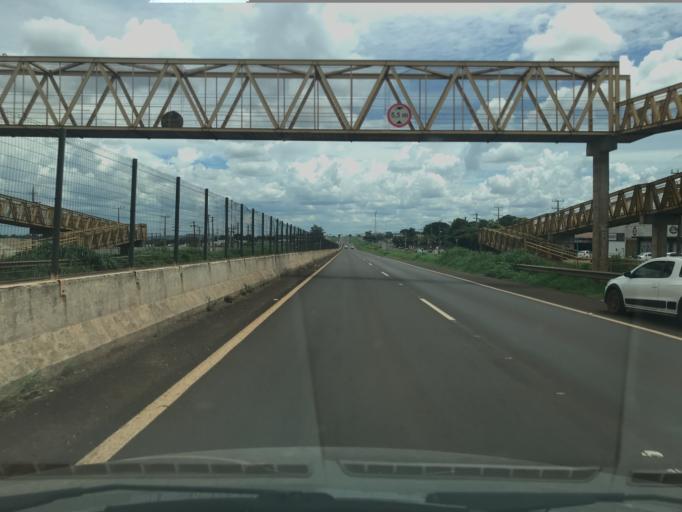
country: BR
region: Parana
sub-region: Paicandu
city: Paicandu
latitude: -23.4610
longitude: -52.0360
